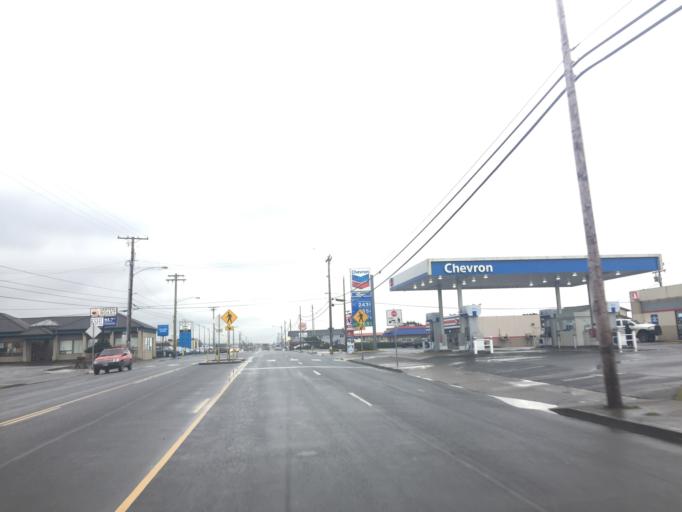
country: US
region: Oregon
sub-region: Lincoln County
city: Newport
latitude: 44.6490
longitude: -124.0531
